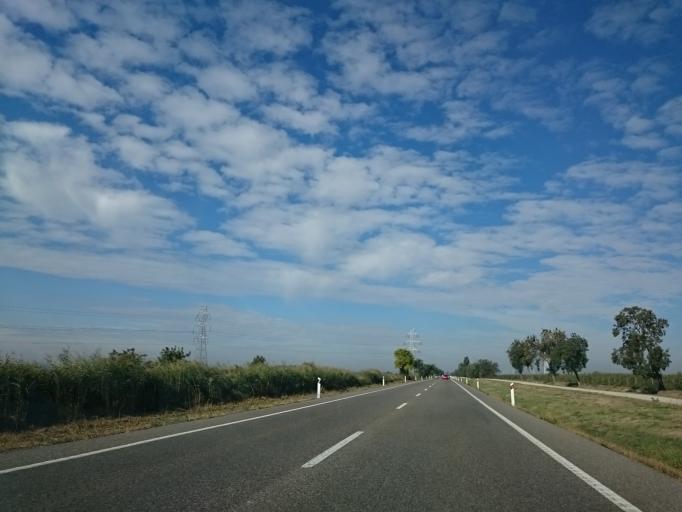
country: ES
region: Catalonia
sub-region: Provincia de Lleida
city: Juneda
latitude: 41.5782
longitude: 0.7530
